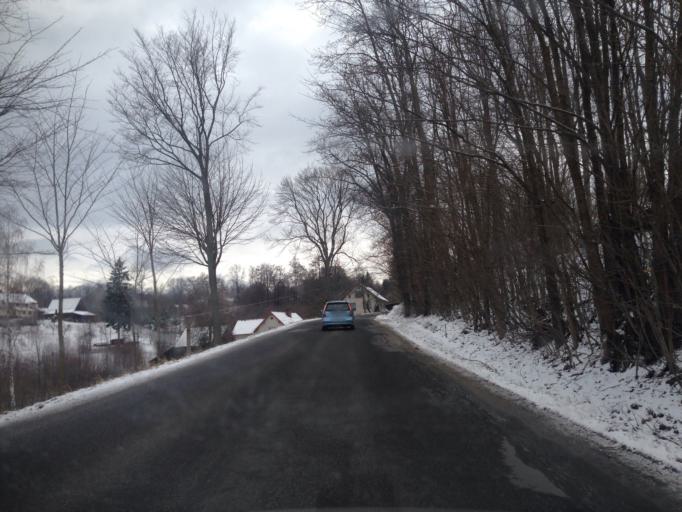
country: CZ
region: Liberecky
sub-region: Okres Semily
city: Vysoke nad Jizerou
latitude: 50.6582
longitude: 15.4159
